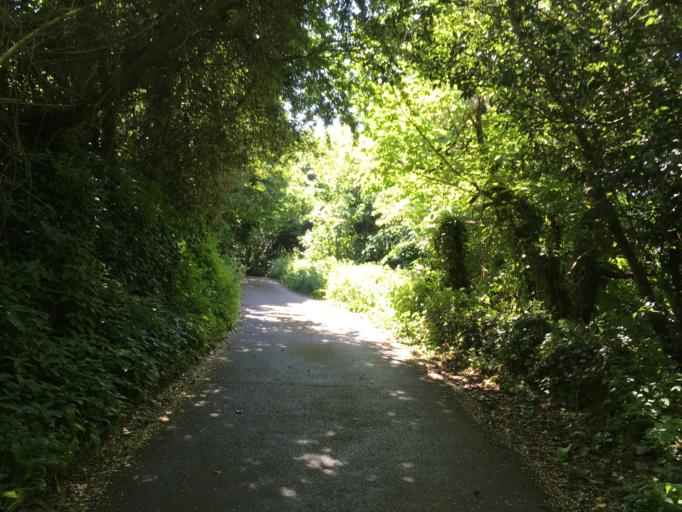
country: GB
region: England
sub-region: Devon
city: Dartmouth
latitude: 50.3451
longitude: -3.5629
